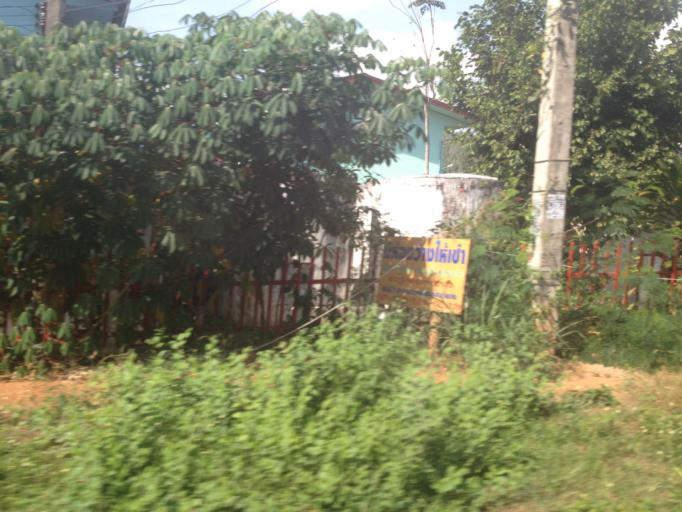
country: TH
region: Chiang Mai
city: Hang Dong
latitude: 18.7520
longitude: 98.8889
